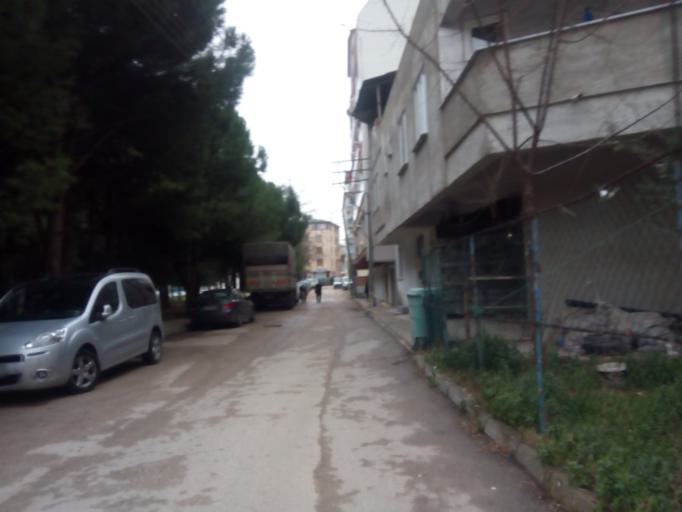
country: TR
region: Bursa
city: Niluefer
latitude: 40.2530
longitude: 28.9617
